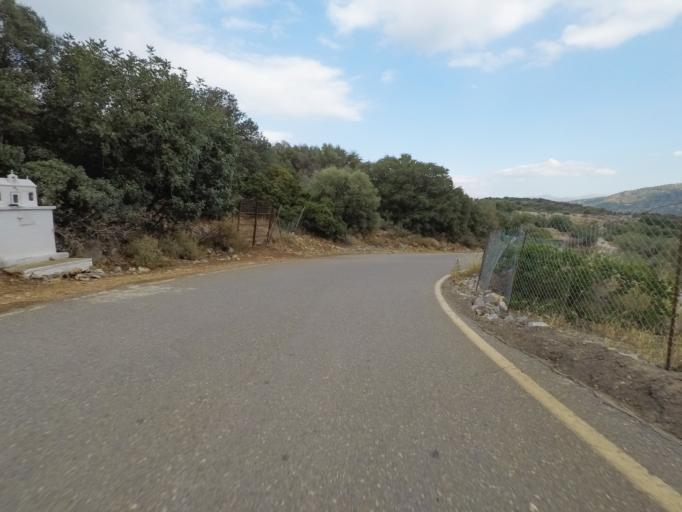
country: GR
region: Crete
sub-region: Nomos Lasithiou
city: Kritsa
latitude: 35.1677
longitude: 25.6551
